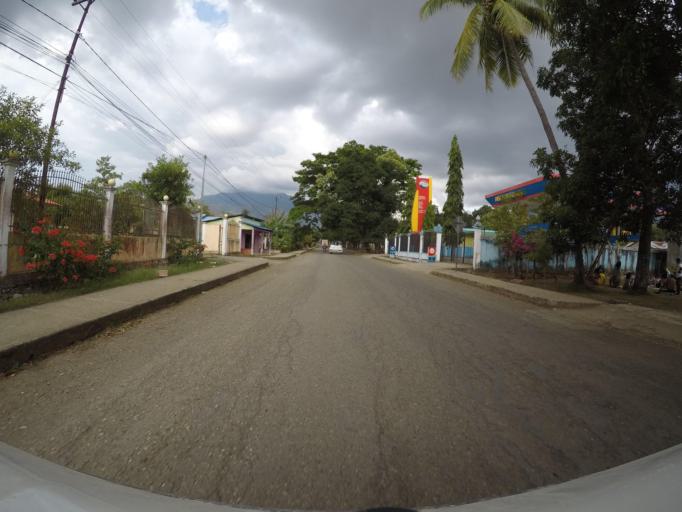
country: TL
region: Bobonaro
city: Maliana
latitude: -8.9909
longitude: 125.1991
